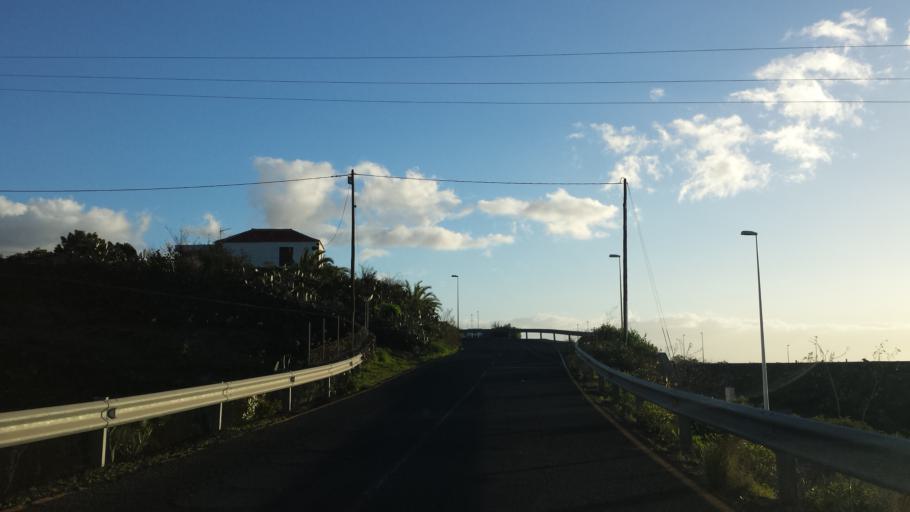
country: ES
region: Canary Islands
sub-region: Provincia de Santa Cruz de Tenerife
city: El Paso
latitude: 28.6262
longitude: -17.8850
